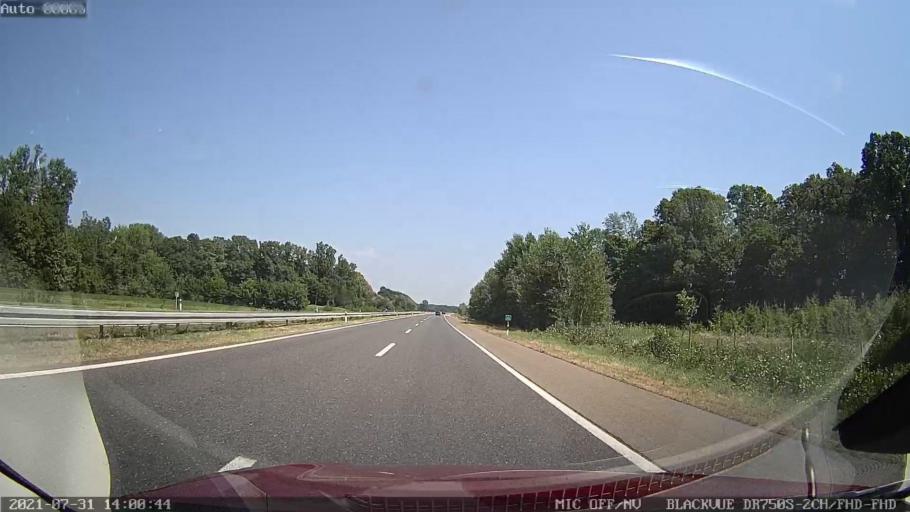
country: HR
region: Brodsko-Posavska
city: Garcin
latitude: 45.1548
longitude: 18.2438
